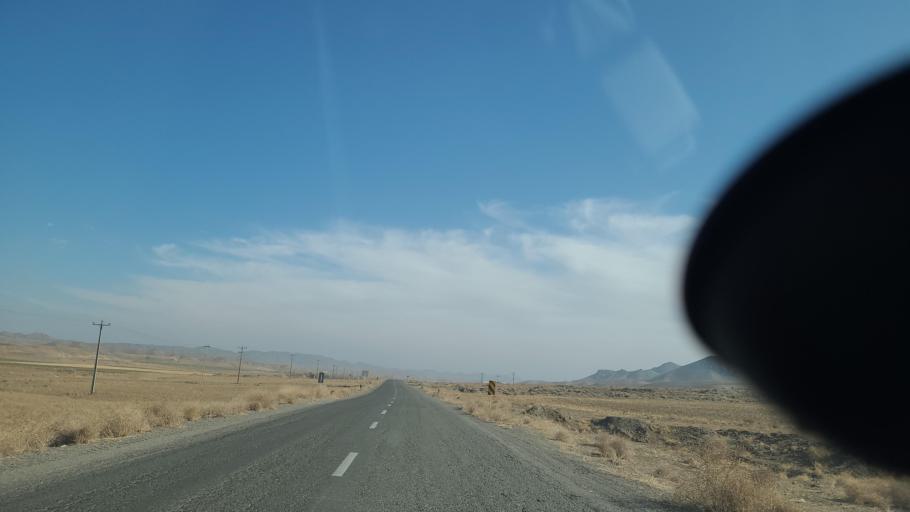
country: IR
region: Razavi Khorasan
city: Fariman
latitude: 35.5874
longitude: 59.6513
